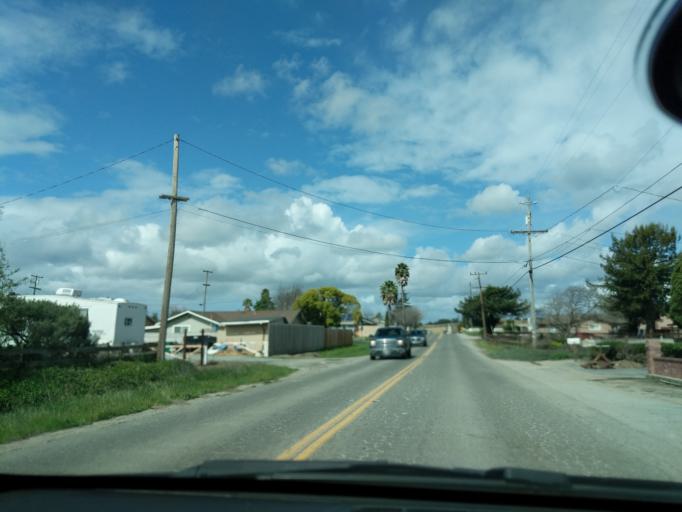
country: US
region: California
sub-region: Monterey County
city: Prunedale
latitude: 36.7579
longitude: -121.6128
